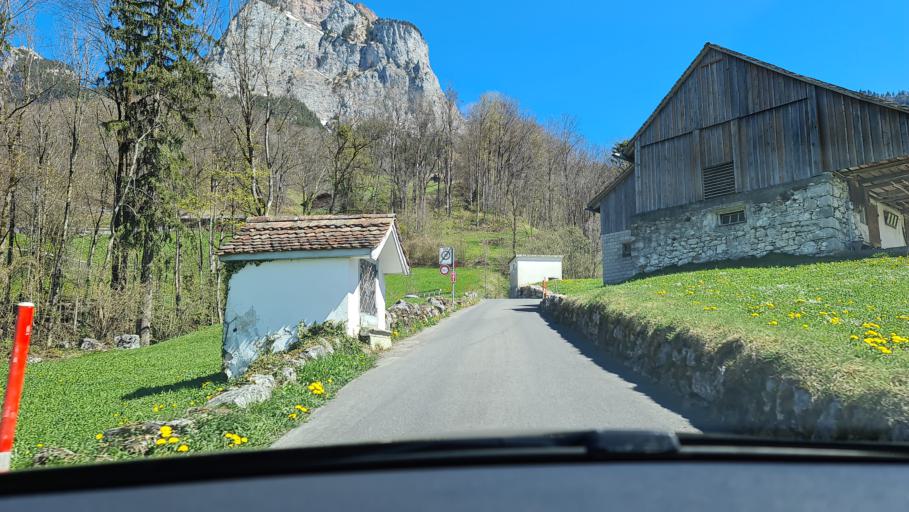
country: CH
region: Schwyz
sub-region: Bezirk Schwyz
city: Schwyz
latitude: 47.0168
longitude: 8.6700
